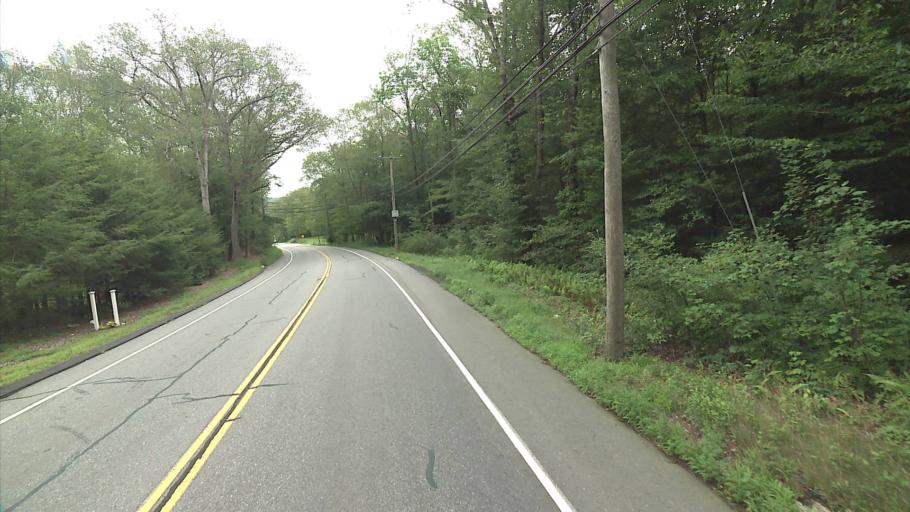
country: US
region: Connecticut
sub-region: Tolland County
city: Storrs
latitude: 41.8729
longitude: -72.2524
